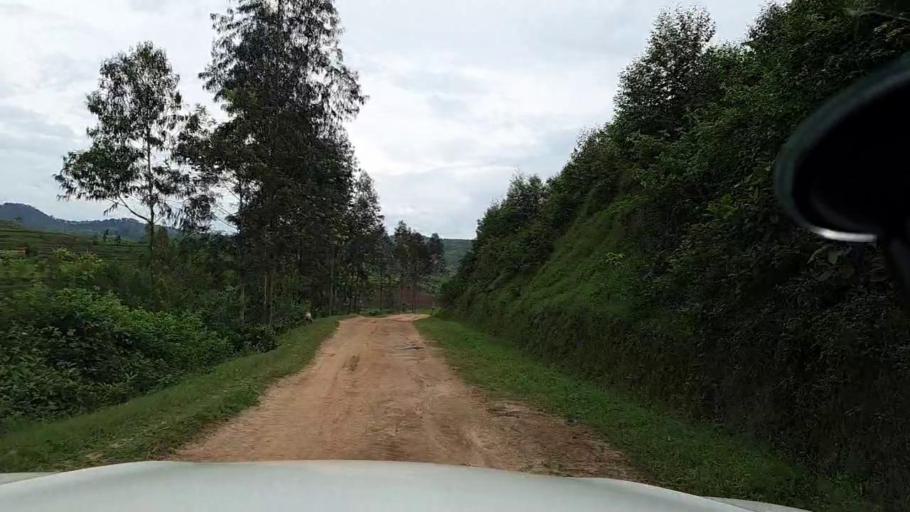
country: RW
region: Southern Province
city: Gitarama
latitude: -2.0920
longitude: 29.6408
